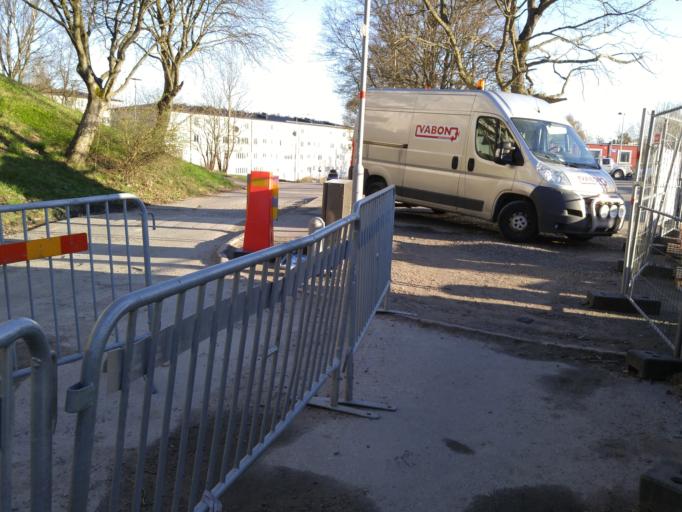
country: SE
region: Vaestra Goetaland
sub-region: Goteborg
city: Majorna
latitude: 57.6724
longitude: 11.9201
